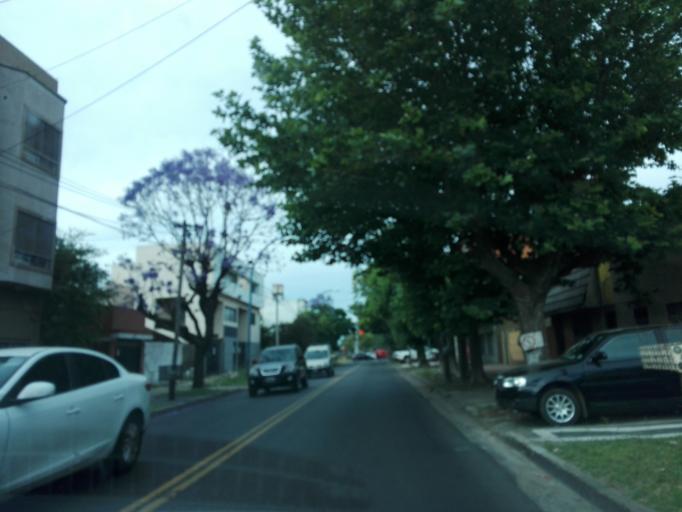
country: AR
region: Buenos Aires
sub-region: Partido de Lanus
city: Lanus
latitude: -34.7074
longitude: -58.3722
